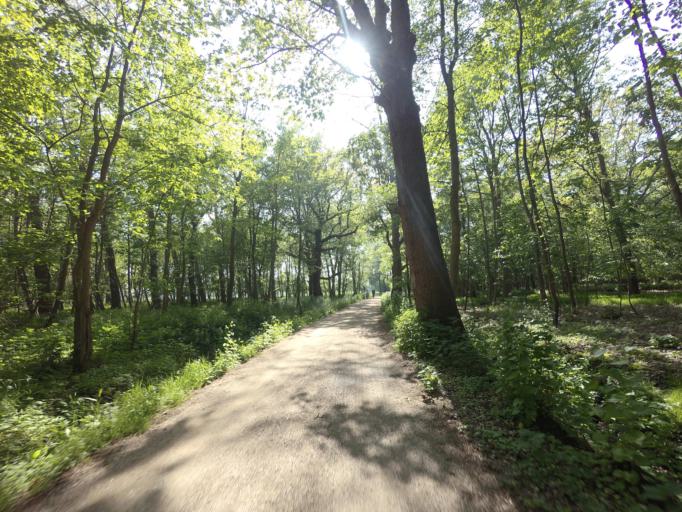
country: NL
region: Zeeland
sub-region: Gemeente Middelburg
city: Middelburg
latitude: 51.5728
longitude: 3.5315
